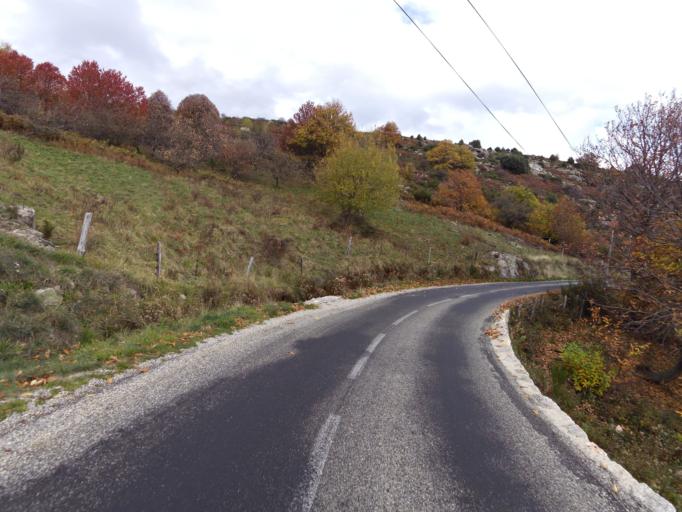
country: FR
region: Rhone-Alpes
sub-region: Departement de l'Ardeche
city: Les Vans
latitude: 44.5084
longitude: 4.0478
